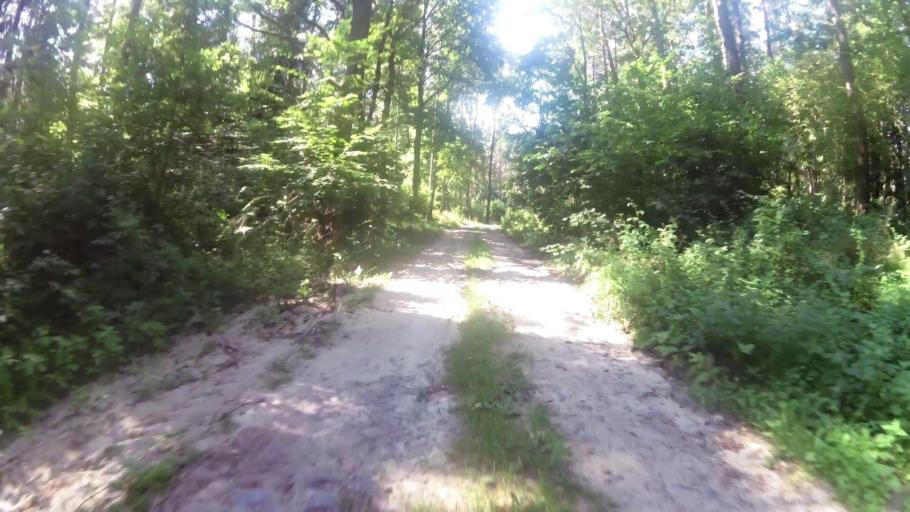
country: PL
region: West Pomeranian Voivodeship
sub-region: Powiat drawski
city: Drawsko Pomorskie
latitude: 53.5336
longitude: 15.7110
